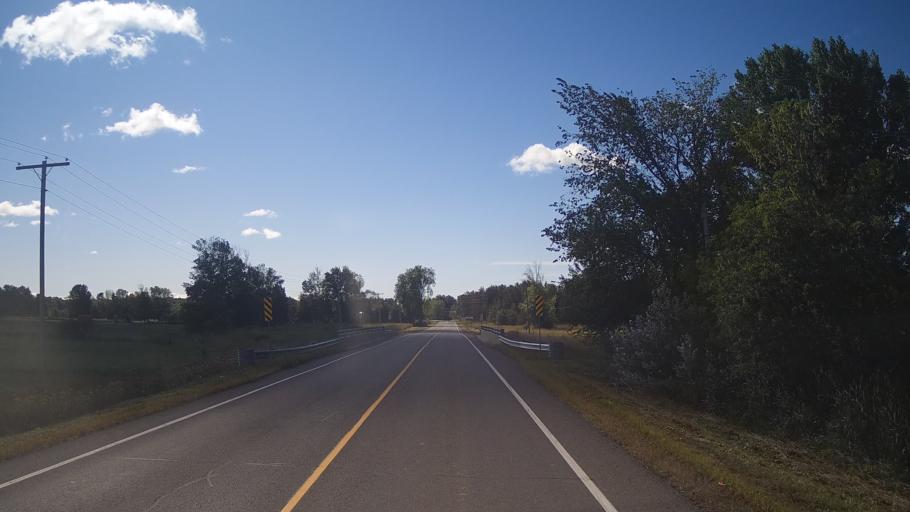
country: CA
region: Ontario
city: Prescott
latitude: 44.9068
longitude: -75.4031
